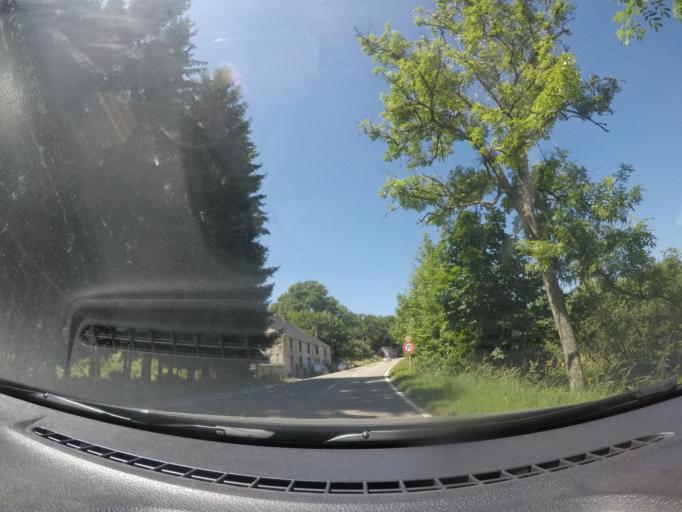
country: BE
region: Wallonia
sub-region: Province du Luxembourg
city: Wellin
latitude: 50.0631
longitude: 5.1382
